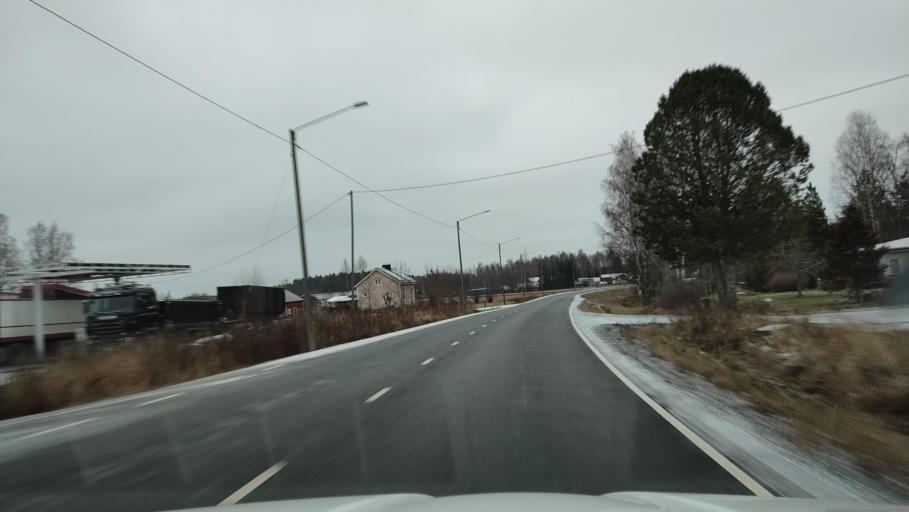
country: FI
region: Southern Ostrobothnia
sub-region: Suupohja
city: Karijoki
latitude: 62.3043
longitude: 21.6923
